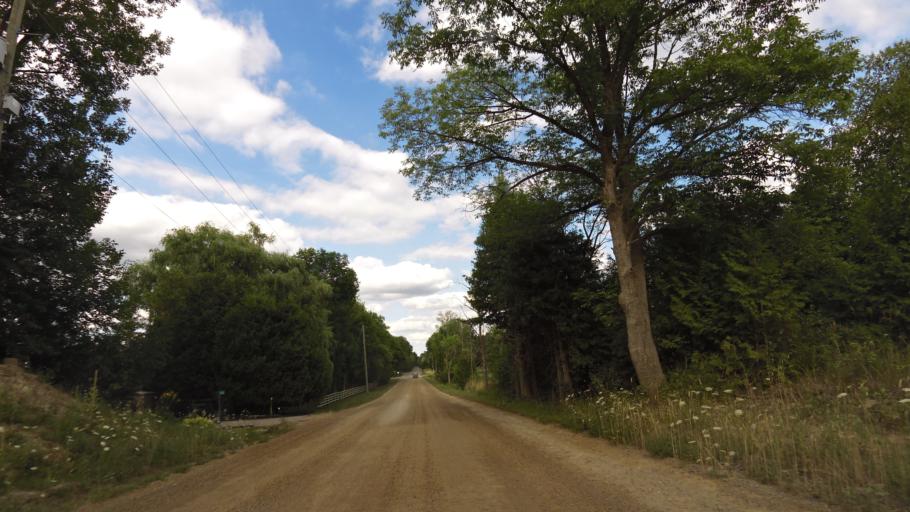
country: CA
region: Ontario
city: Orangeville
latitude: 43.9814
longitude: -79.9443
